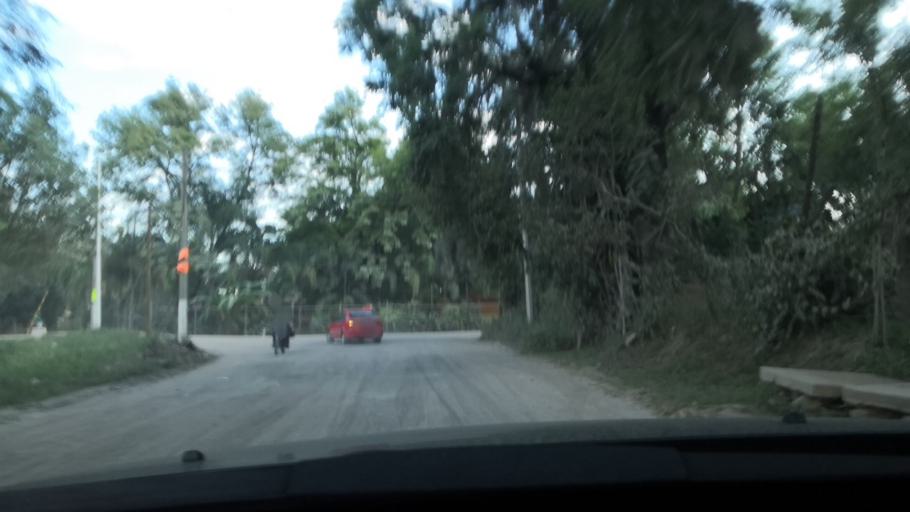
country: MX
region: Guanajuato
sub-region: San Francisco del Rincon
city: Fraccionamiento la Mezquitera
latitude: 21.0215
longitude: -101.8405
